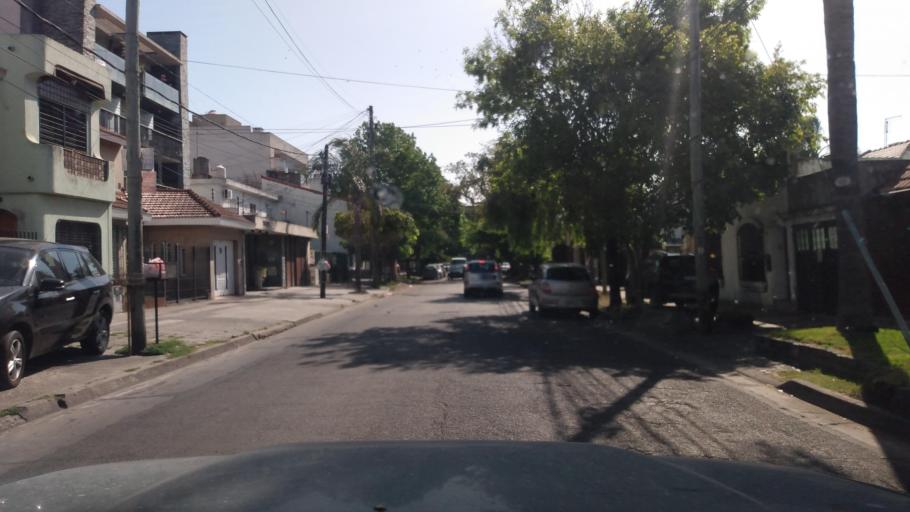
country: AR
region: Buenos Aires
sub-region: Partido de Moron
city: Moron
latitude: -34.6475
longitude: -58.5905
